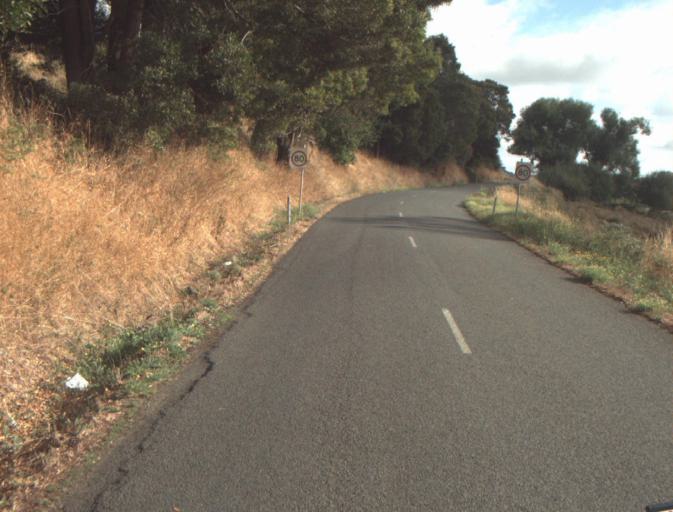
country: AU
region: Tasmania
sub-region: Launceston
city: Mayfield
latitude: -41.1855
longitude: 147.2218
